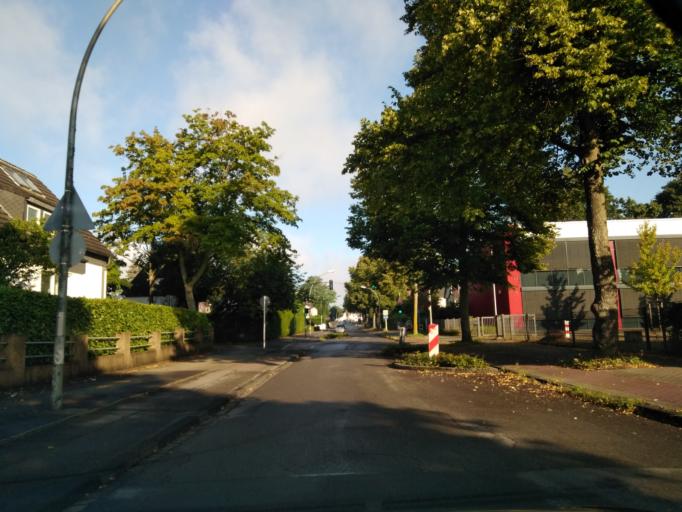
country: DE
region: North Rhine-Westphalia
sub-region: Regierungsbezirk Munster
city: Gelsenkirchen
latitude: 51.5586
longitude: 7.0860
